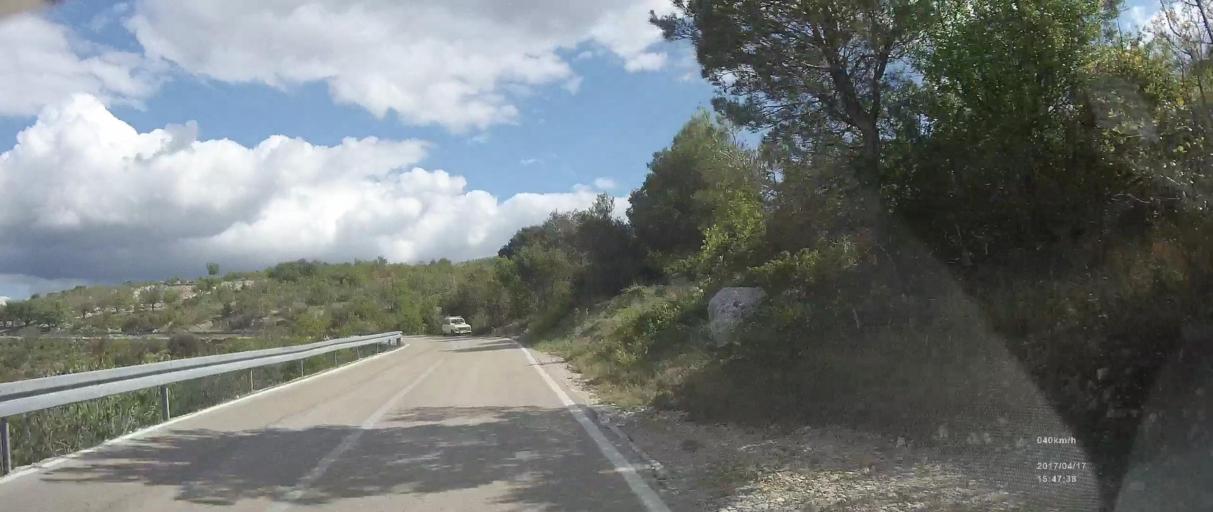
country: HR
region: Sibensko-Kniniska
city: Primosten
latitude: 43.6224
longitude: 15.9785
